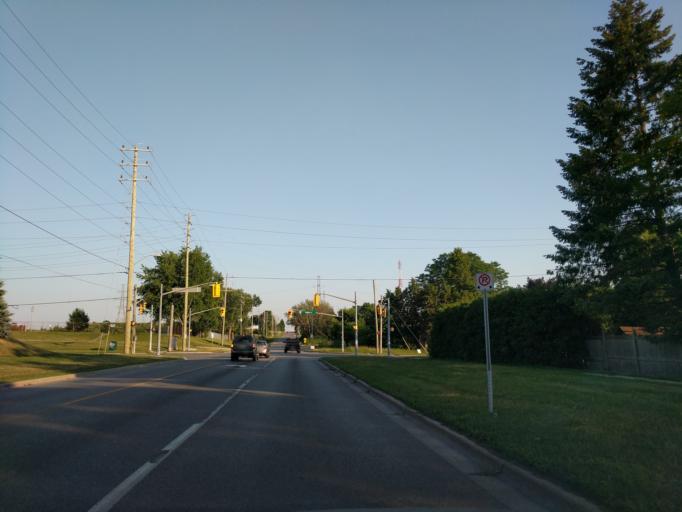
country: CA
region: Ontario
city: Oshawa
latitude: 43.8844
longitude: -78.8901
